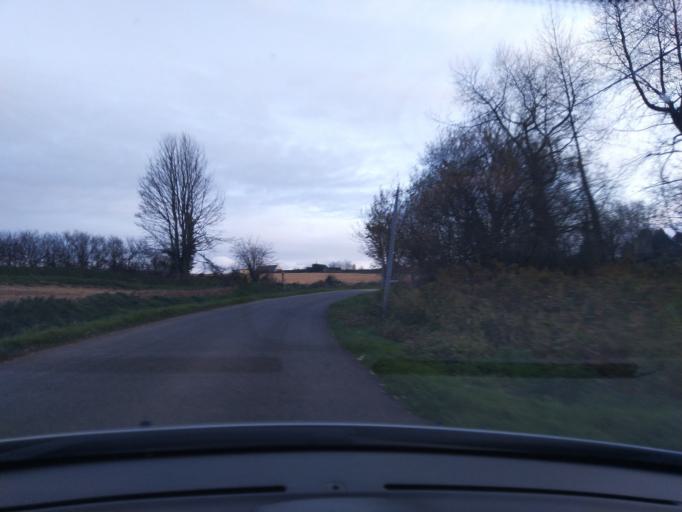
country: FR
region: Brittany
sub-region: Departement du Finistere
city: Guerlesquin
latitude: 48.5219
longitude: -3.5969
